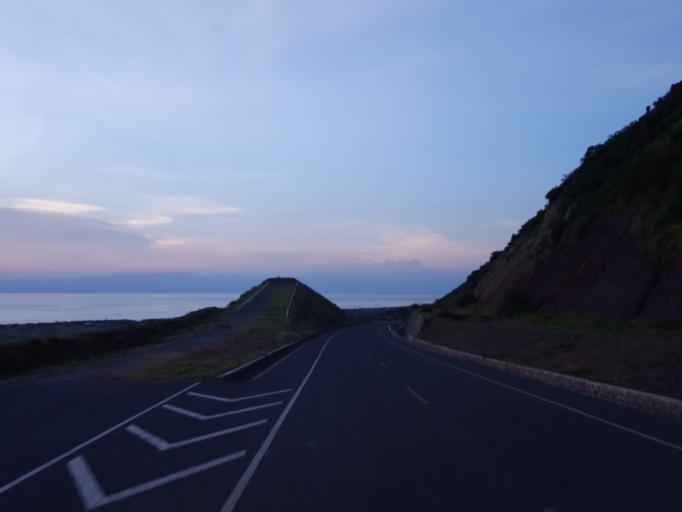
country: UG
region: Western Region
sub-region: Kibale District
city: Kagadi
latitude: 1.2478
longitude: 30.7586
